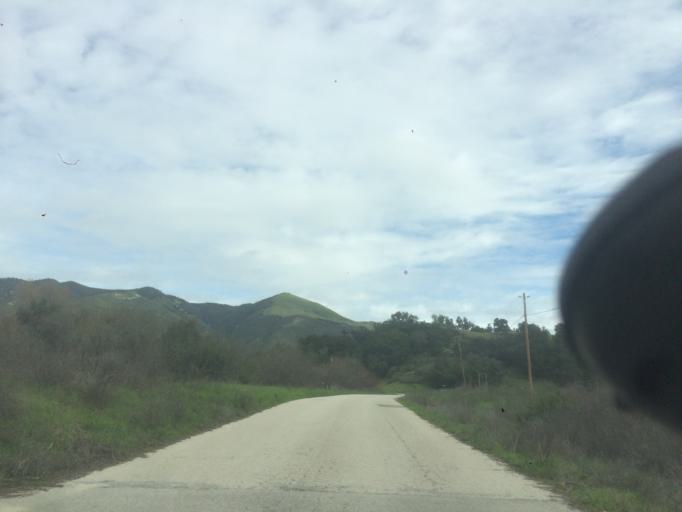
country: US
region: California
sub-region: San Luis Obispo County
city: Nipomo
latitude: 35.2036
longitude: -120.4214
